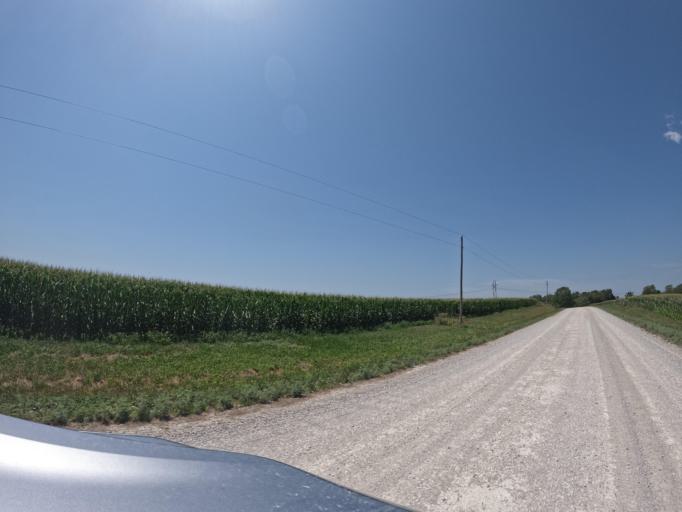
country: US
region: Iowa
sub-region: Henry County
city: Mount Pleasant
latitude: 40.9386
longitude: -91.6361
